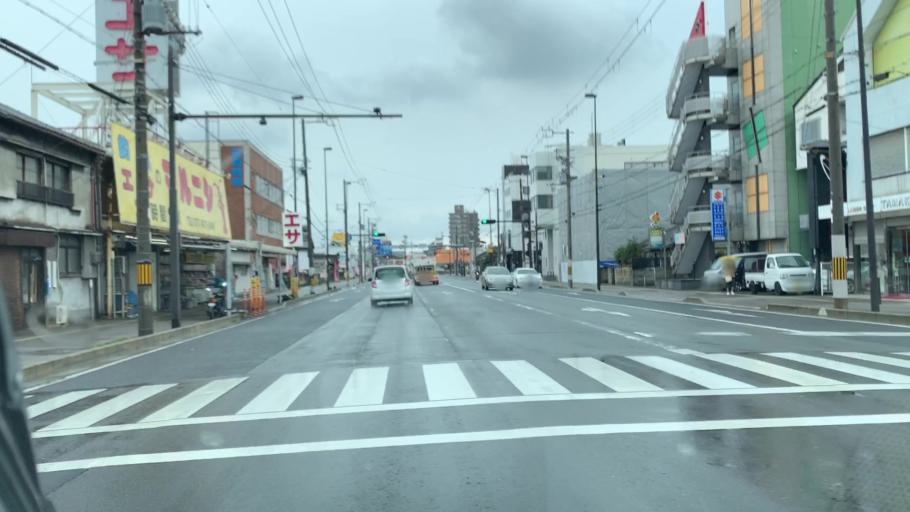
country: JP
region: Wakayama
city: Wakayama-shi
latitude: 34.2264
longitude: 135.1602
